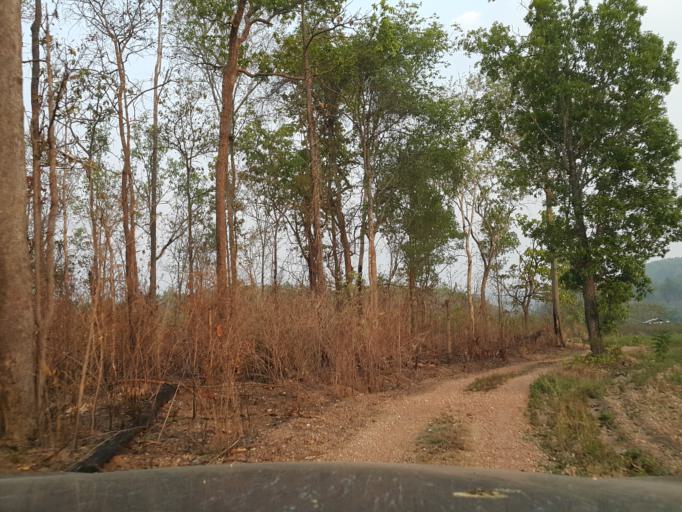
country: TH
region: Lamphun
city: Thung Hua Chang
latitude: 17.9155
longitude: 99.0734
